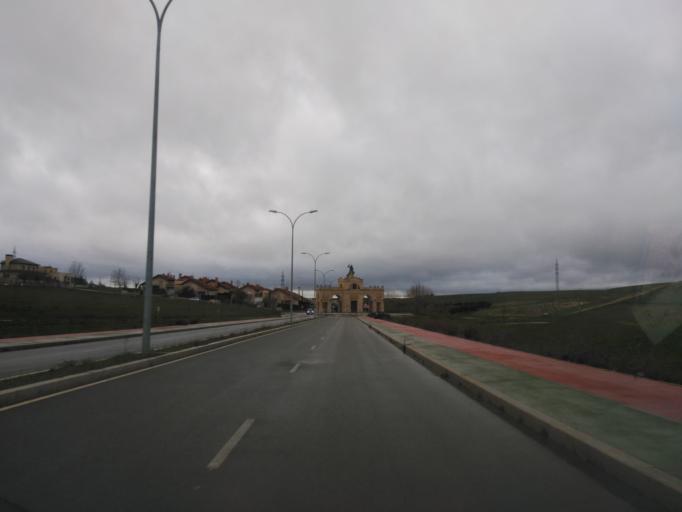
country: ES
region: Castille and Leon
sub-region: Provincia de Salamanca
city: Villamayor
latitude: 40.9806
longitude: -5.6931
